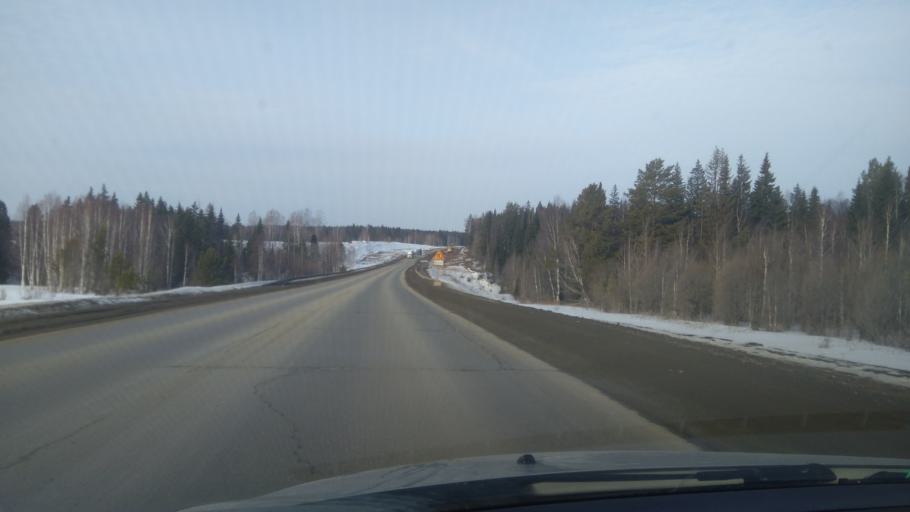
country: RU
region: Sverdlovsk
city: Bisert'
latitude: 56.8257
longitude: 59.1689
